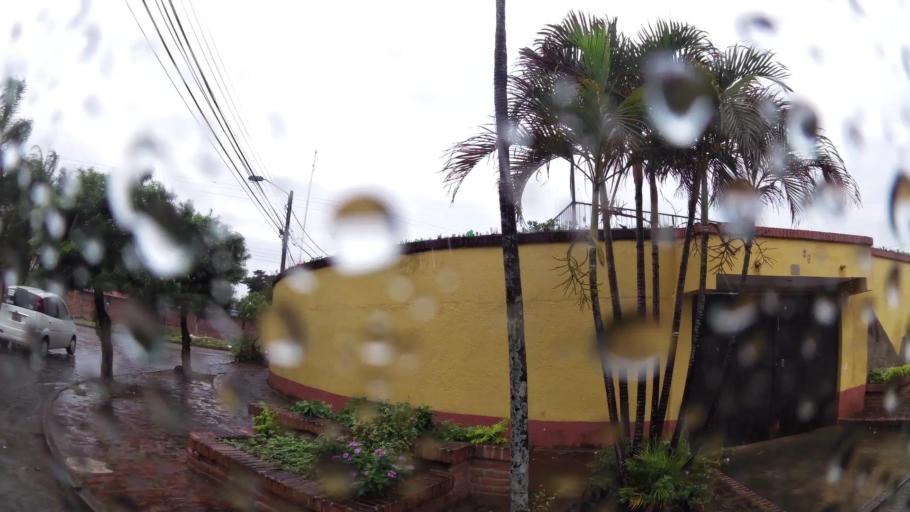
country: BO
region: Santa Cruz
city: Santa Cruz de la Sierra
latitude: -17.7975
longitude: -63.1649
